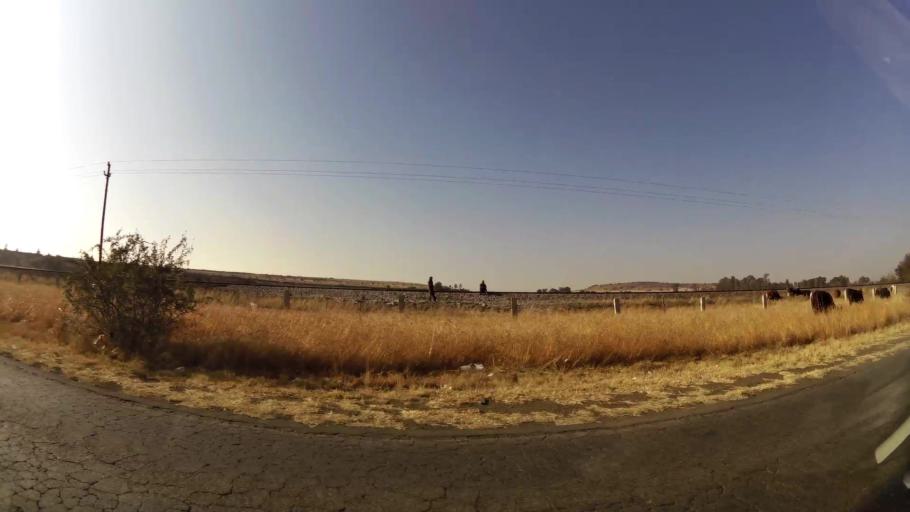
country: ZA
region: Orange Free State
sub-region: Mangaung Metropolitan Municipality
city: Bloemfontein
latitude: -29.1829
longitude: 26.1881
